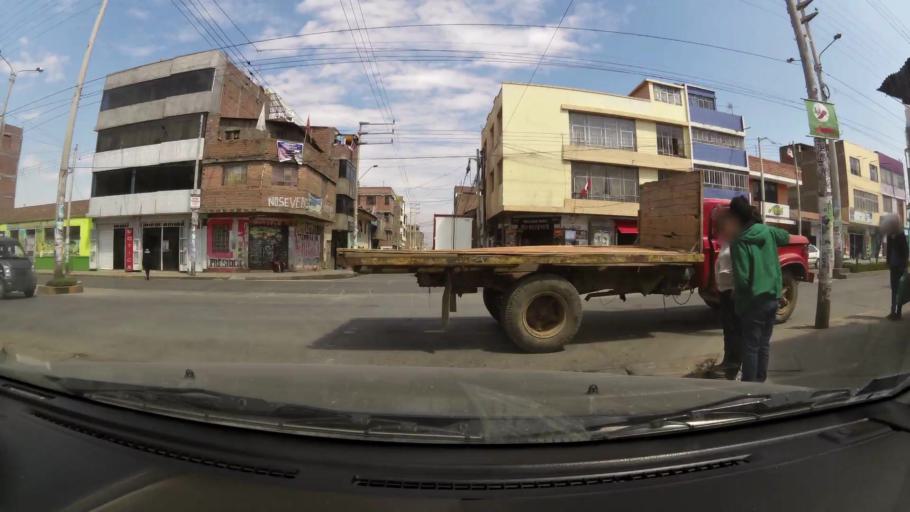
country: PE
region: Junin
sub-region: Provincia de Huancayo
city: El Tambo
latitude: -12.0723
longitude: -75.2134
